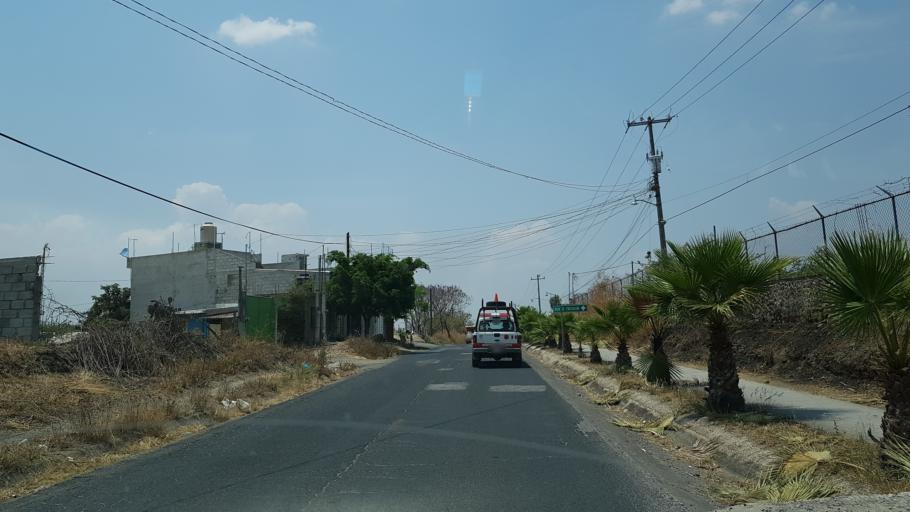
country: MX
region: Morelos
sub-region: Yecapixtla
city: Yecapixtla
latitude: 18.8769
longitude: -98.8697
